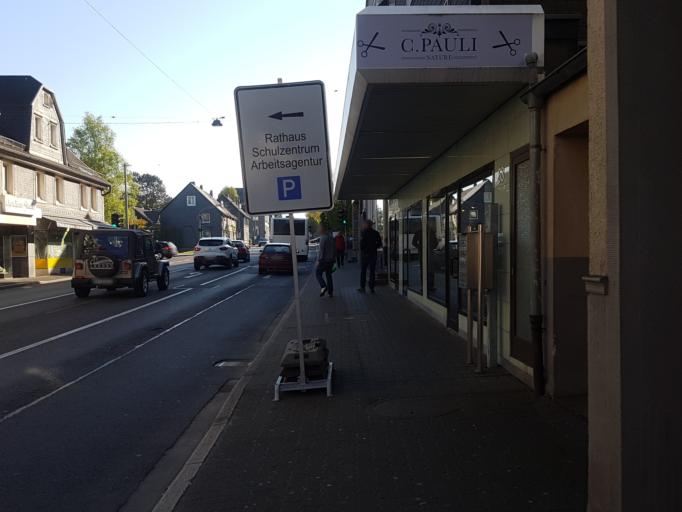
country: DE
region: North Rhine-Westphalia
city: Waldbrol
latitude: 50.8776
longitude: 7.6202
